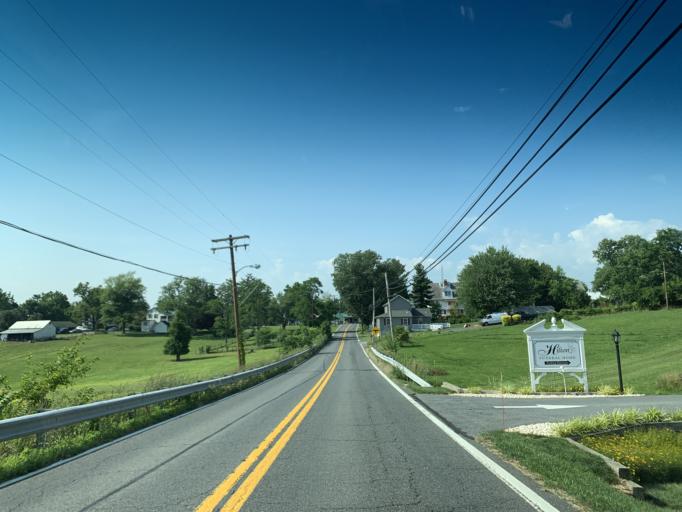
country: US
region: Maryland
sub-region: Montgomery County
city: Poolesville
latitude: 39.2189
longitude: -77.3778
